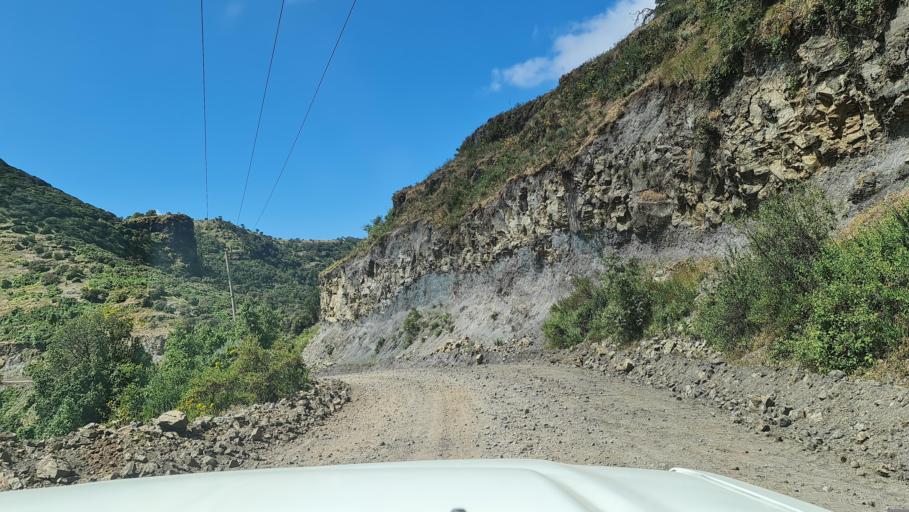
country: ET
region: Amhara
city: Debark'
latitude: 13.2309
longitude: 38.0319
